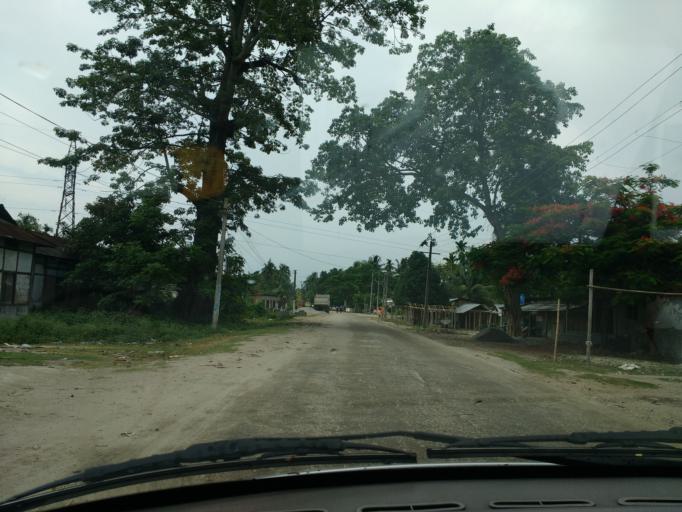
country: IN
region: Assam
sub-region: Udalguri
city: Udalguri
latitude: 26.7329
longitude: 92.2154
